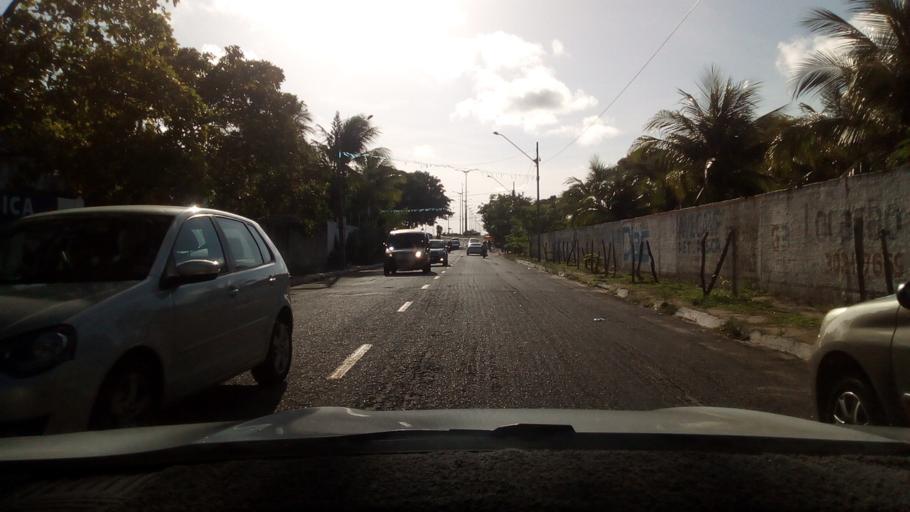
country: BR
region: Paraiba
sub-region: Joao Pessoa
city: Joao Pessoa
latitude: -7.1613
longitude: -34.7986
